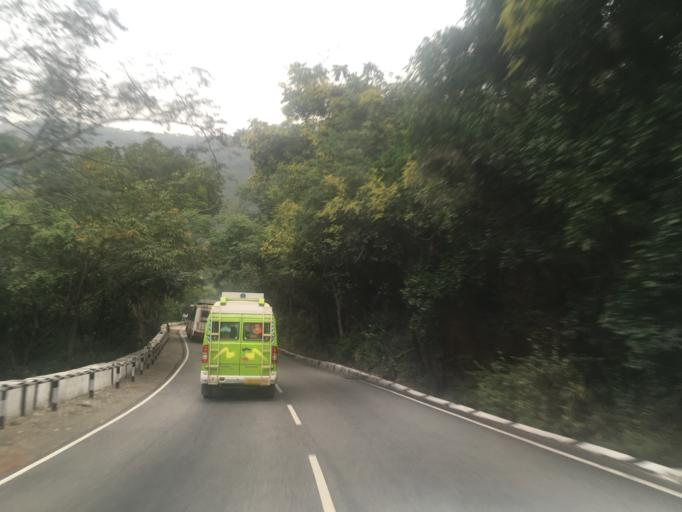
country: IN
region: Andhra Pradesh
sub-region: Chittoor
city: Tirumala
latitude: 13.6600
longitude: 79.3499
